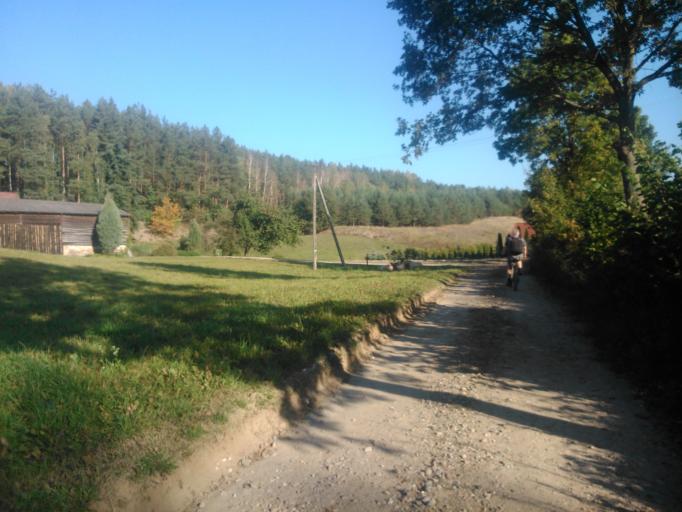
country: PL
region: Kujawsko-Pomorskie
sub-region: Powiat brodnicki
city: Gorzno
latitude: 53.2115
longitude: 19.6480
